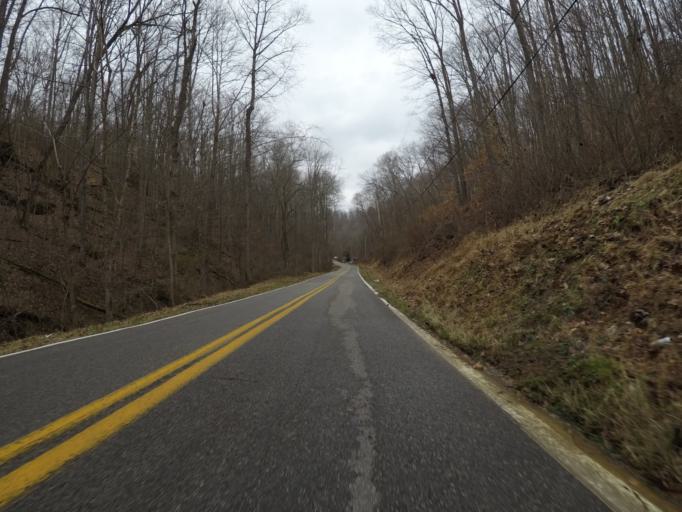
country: US
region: West Virginia
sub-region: Cabell County
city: Barboursville
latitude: 38.4576
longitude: -82.2674
